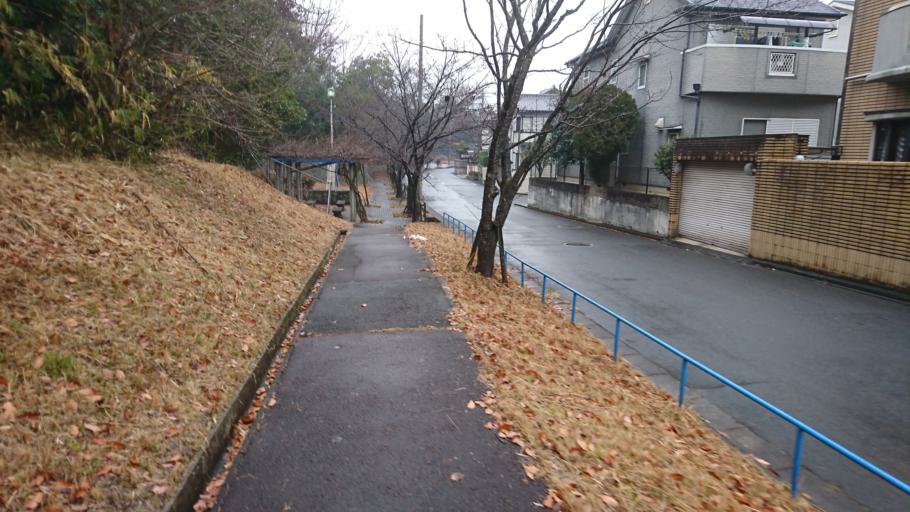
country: JP
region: Nara
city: Nara-shi
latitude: 34.7096
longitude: 135.8027
